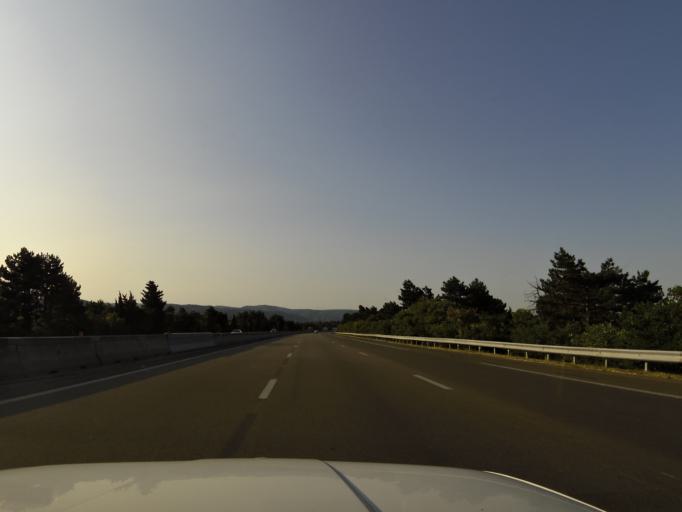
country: FR
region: Rhone-Alpes
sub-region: Departement de la Drome
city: Loriol-sur-Drome
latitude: 44.7412
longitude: 4.7893
